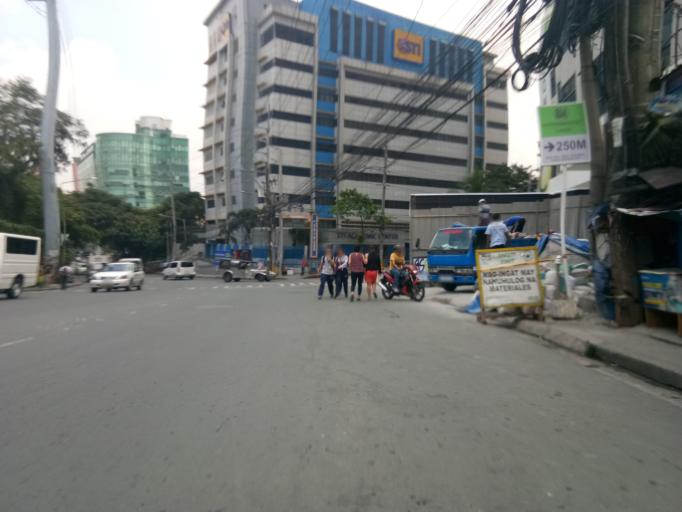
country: PH
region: Metro Manila
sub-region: San Juan
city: San Juan
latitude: 14.6164
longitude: 121.0532
